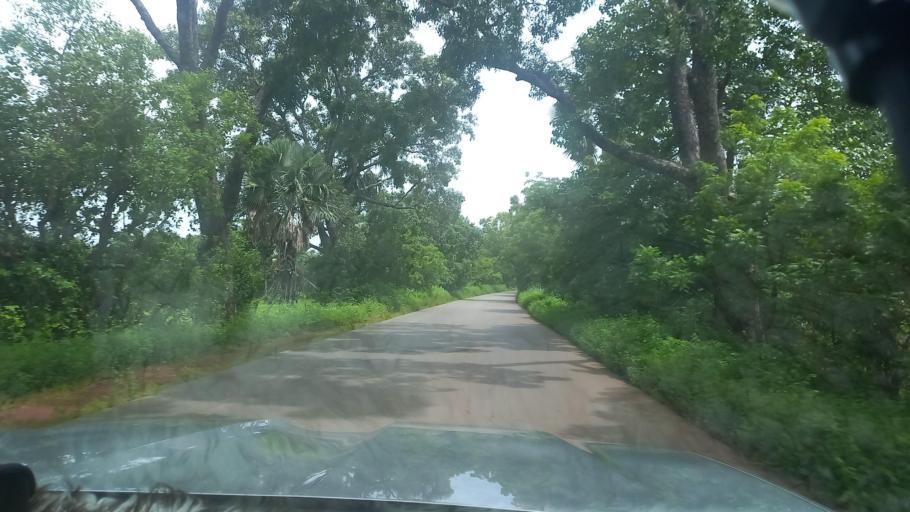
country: SN
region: Kolda
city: Marsassoum
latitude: 12.9576
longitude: -16.0025
